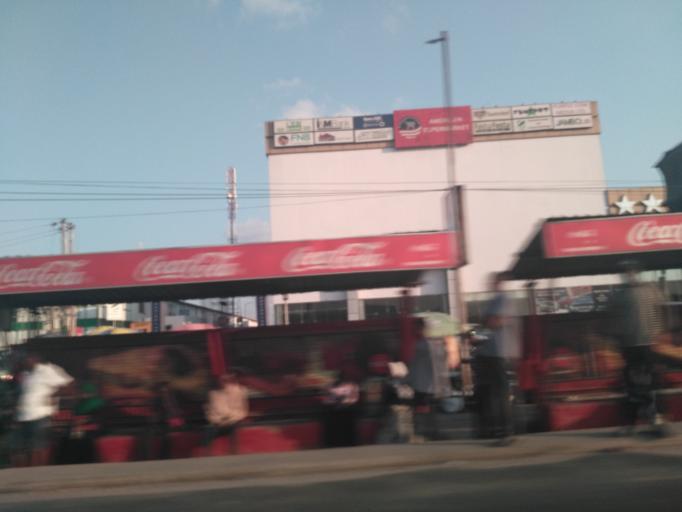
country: TZ
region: Dar es Salaam
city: Dar es Salaam
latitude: -6.8391
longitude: 39.2559
